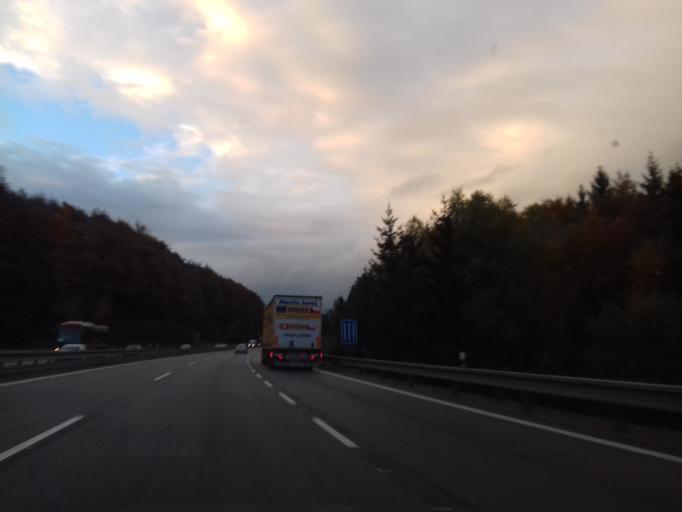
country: CZ
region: Vysocina
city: Stoky
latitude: 49.4700
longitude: 15.5686
